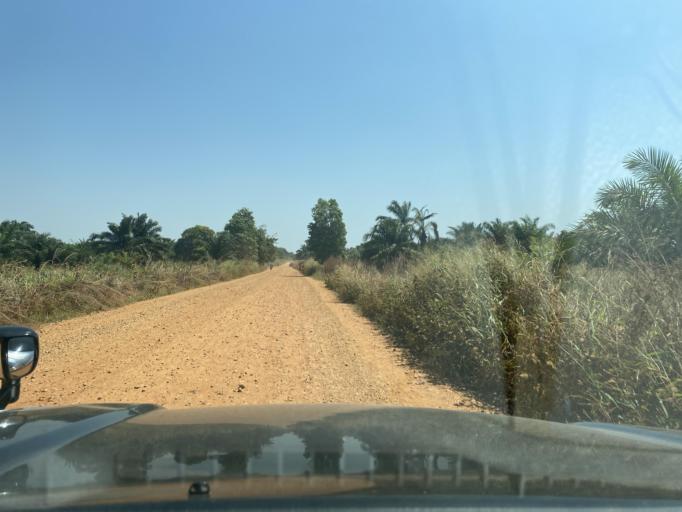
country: CD
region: Kasai-Oriental
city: Mbuji-Mayi
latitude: -6.2579
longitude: 23.7683
